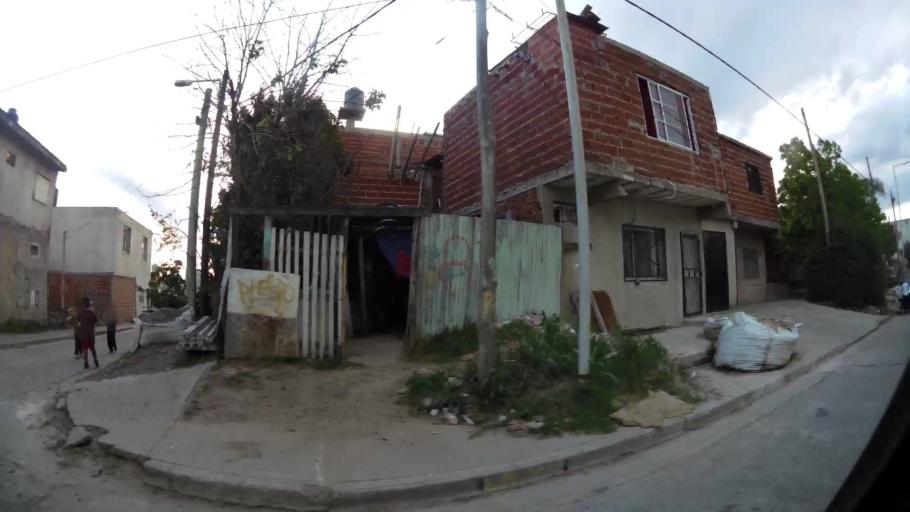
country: AR
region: Buenos Aires
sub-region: Partido de Avellaneda
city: Avellaneda
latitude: -34.6824
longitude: -58.3229
